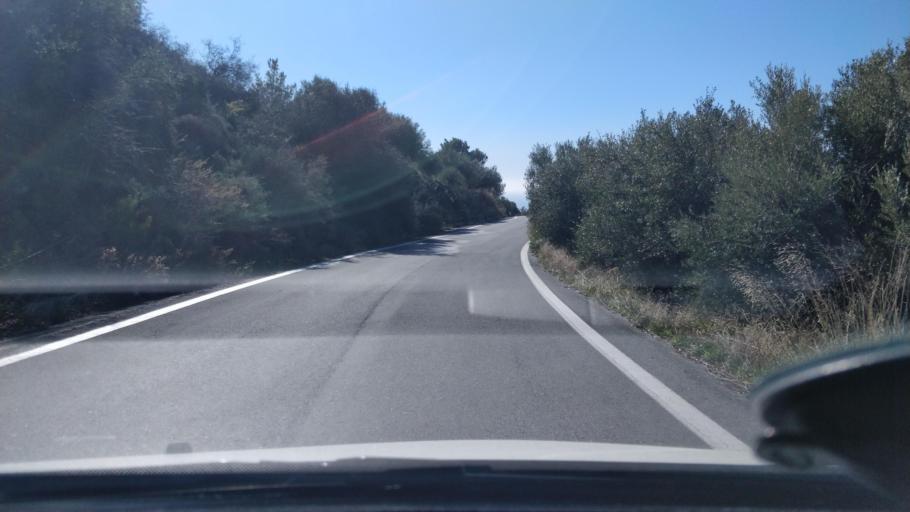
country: GR
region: Crete
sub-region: Nomos Irakleiou
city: Kastelli
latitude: 35.0267
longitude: 25.4492
